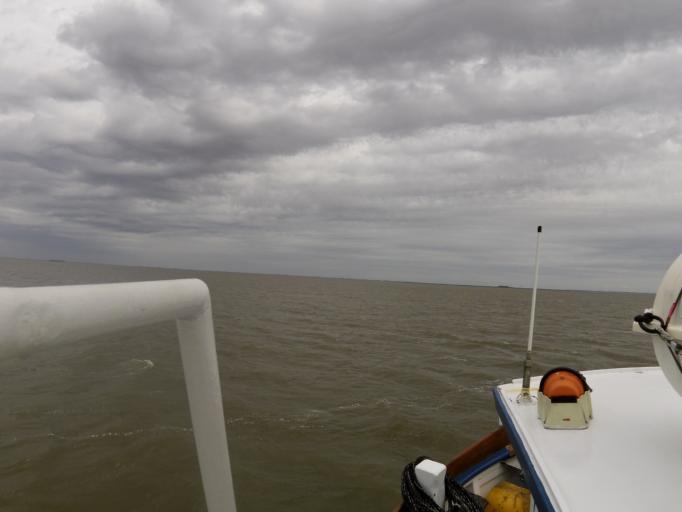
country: DE
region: Schleswig-Holstein
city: Grode
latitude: 54.6168
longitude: 8.6545
